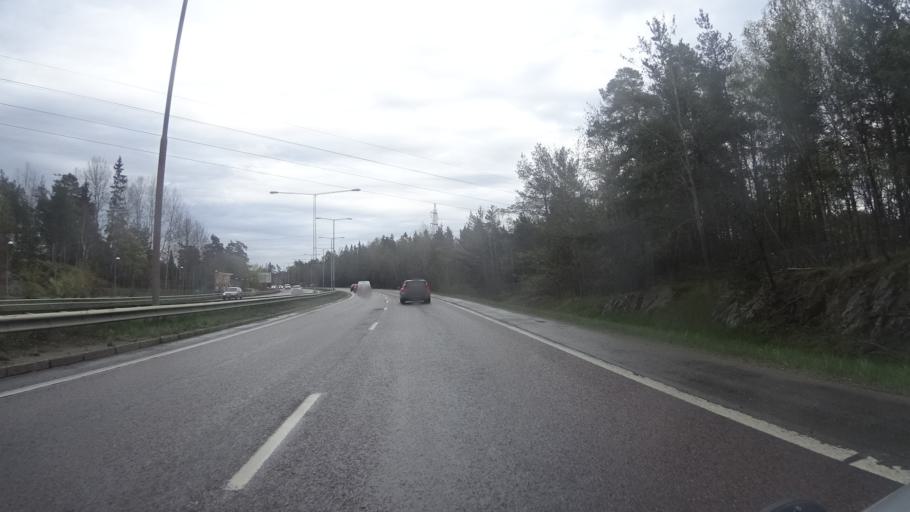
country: SE
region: Stockholm
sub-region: Stockholms Kommun
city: Arsta
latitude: 59.2623
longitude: 18.0649
